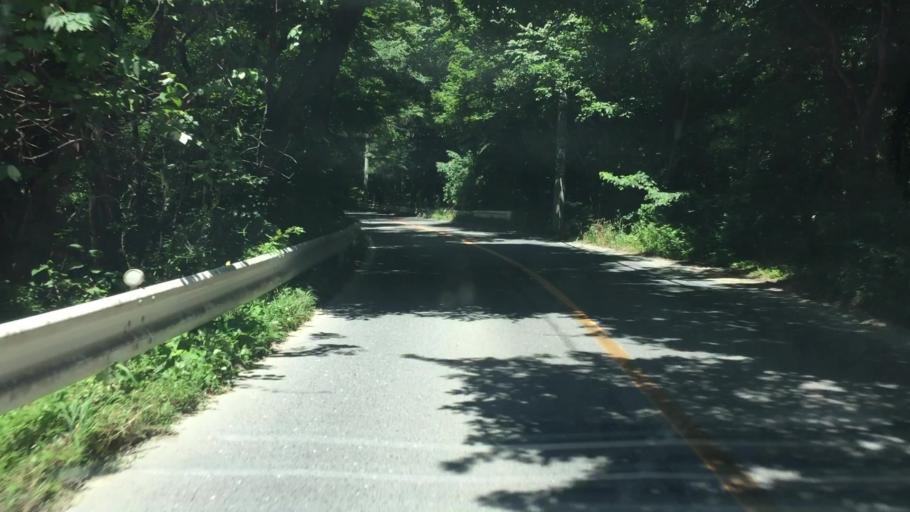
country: JP
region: Tochigi
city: Kuroiso
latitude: 37.0250
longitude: 140.0042
